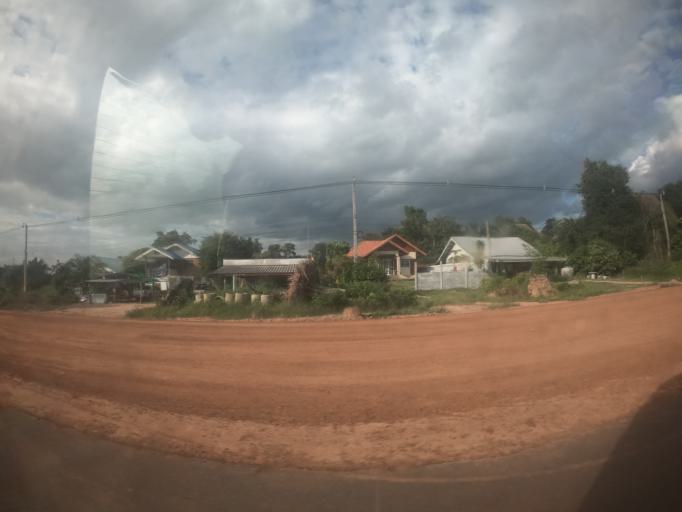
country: TH
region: Surin
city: Kap Choeng
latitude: 14.5007
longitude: 103.5633
